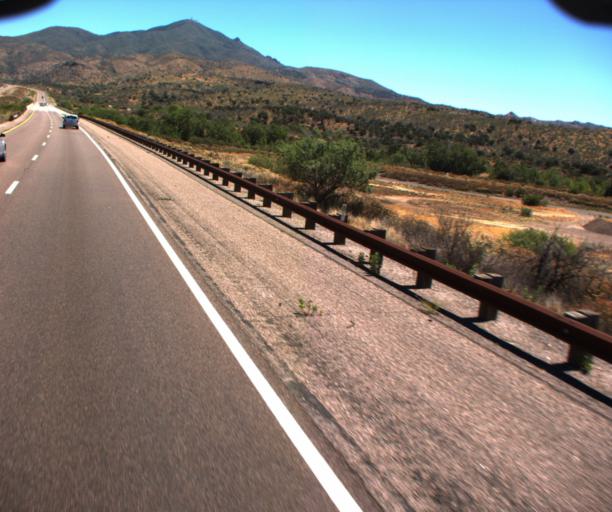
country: US
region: Arizona
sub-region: Gila County
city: Tonto Basin
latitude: 33.8660
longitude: -111.4690
